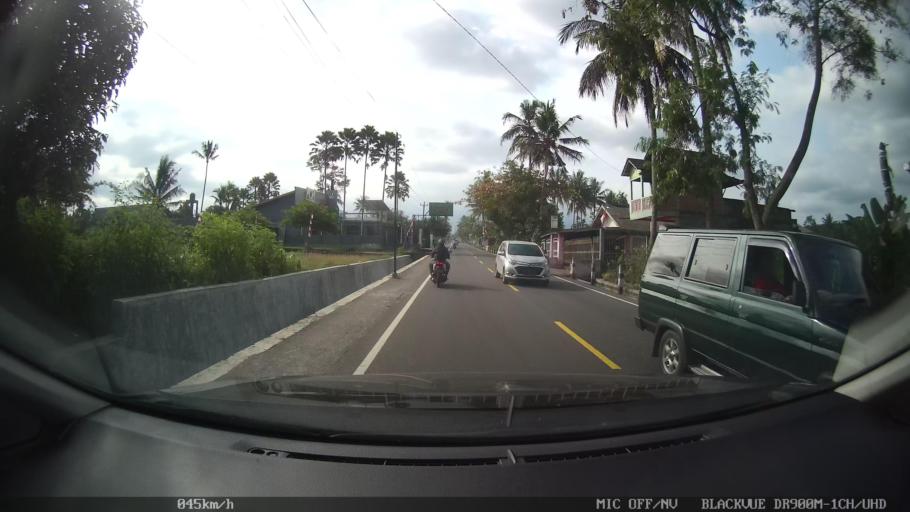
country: ID
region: Central Java
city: Candi Prambanan
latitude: -7.6936
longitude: 110.4632
